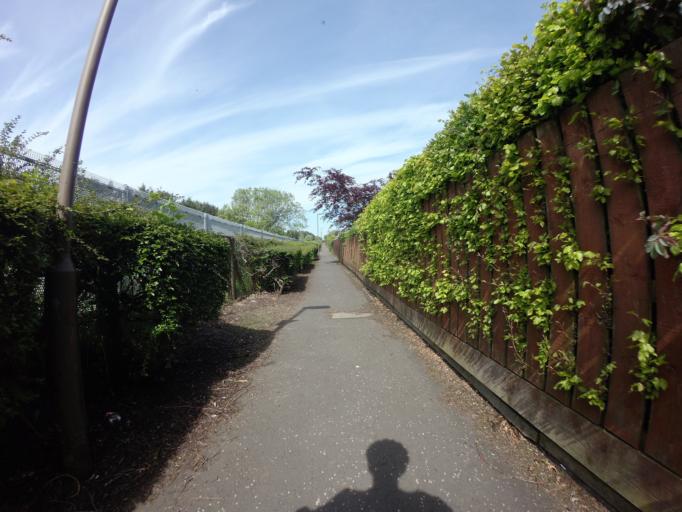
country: GB
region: Scotland
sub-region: West Lothian
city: Livingston
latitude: 55.9088
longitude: -3.5309
